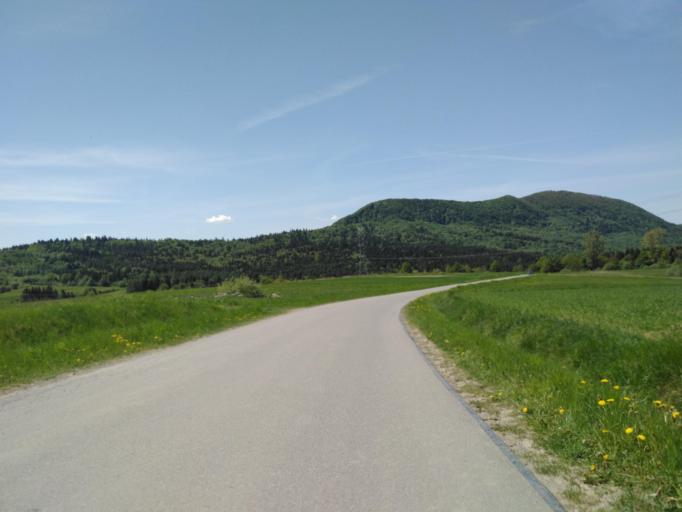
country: PL
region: Subcarpathian Voivodeship
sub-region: Powiat krosnienski
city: Iwonicz-Zdroj
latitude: 49.5374
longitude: 21.7544
